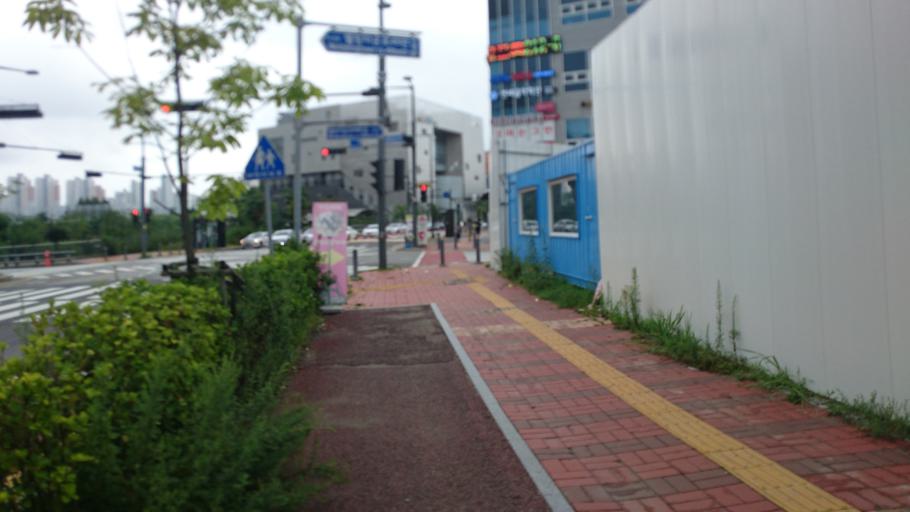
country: KR
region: Gyeonggi-do
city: Suwon-si
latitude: 37.3045
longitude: 127.0474
